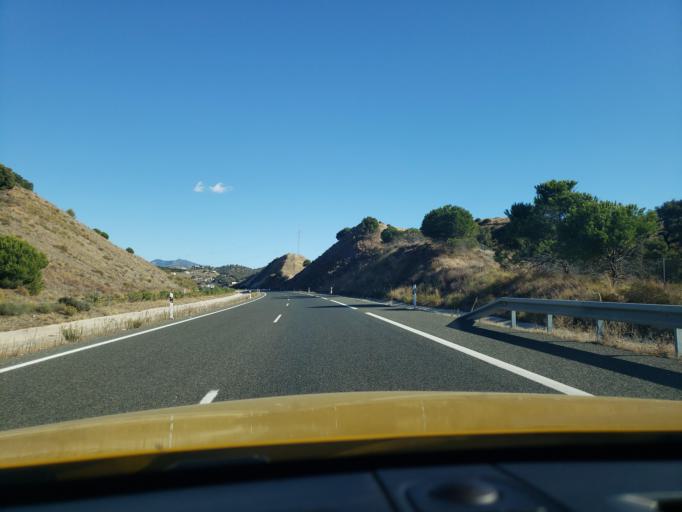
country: ES
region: Andalusia
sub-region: Provincia de Malaga
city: Fuengirola
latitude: 36.5177
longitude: -4.6906
